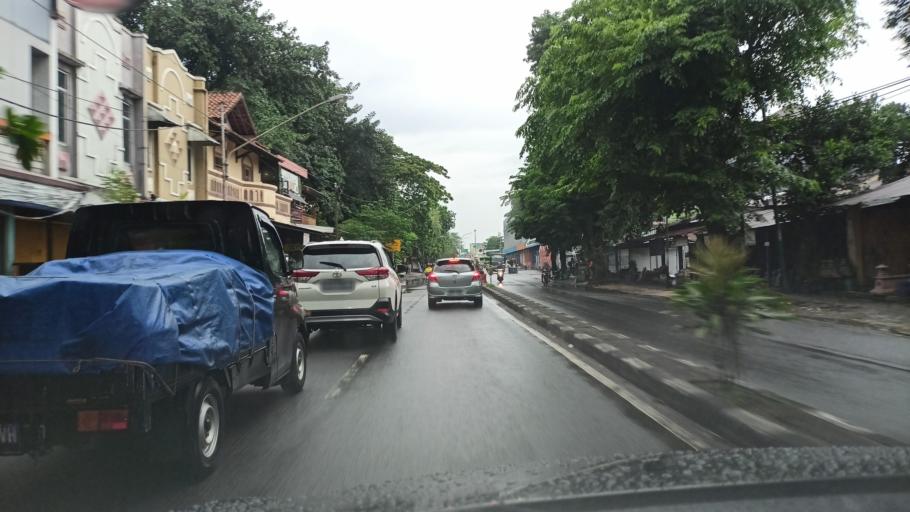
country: ID
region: Central Java
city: Surakarta
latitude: -7.5504
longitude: 110.8169
